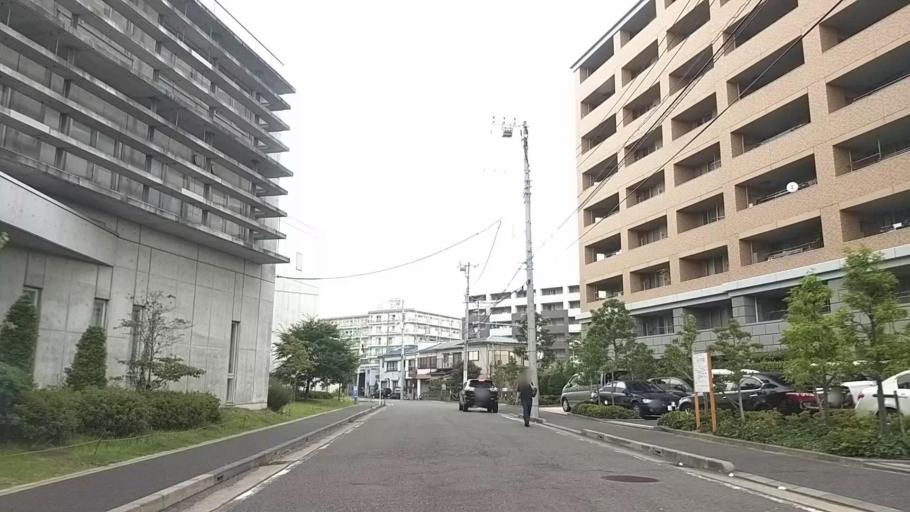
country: JP
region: Kanagawa
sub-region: Kawasaki-shi
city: Kawasaki
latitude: 35.4984
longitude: 139.6791
